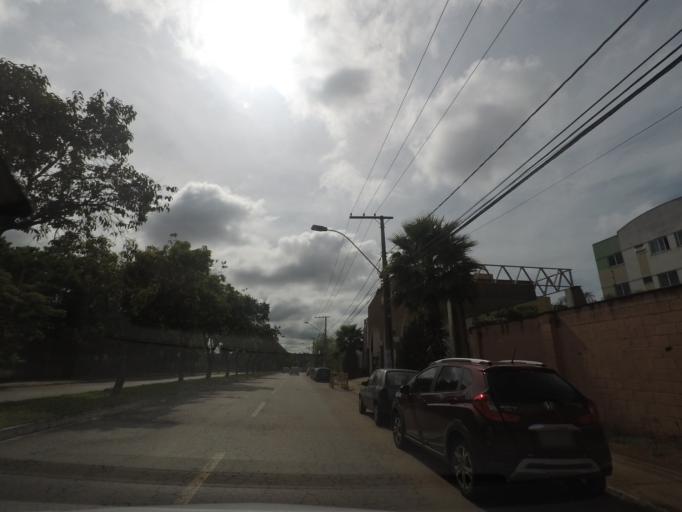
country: BR
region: Goias
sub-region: Goiania
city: Goiania
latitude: -16.6596
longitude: -49.2135
